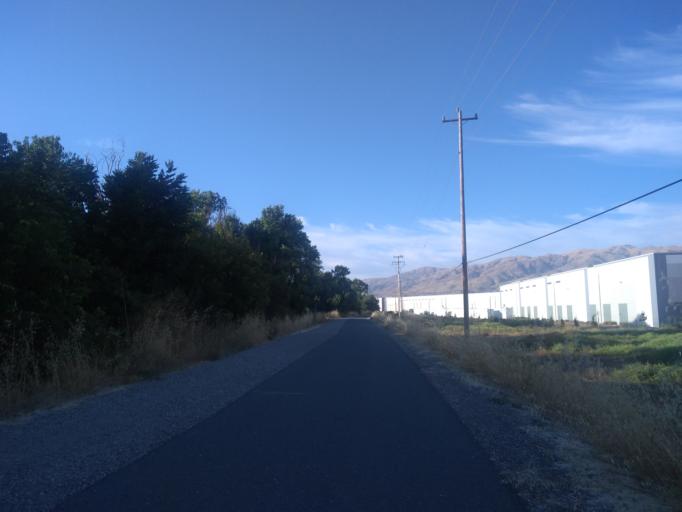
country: US
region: California
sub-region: Santa Clara County
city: Milpitas
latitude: 37.4332
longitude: -121.9269
